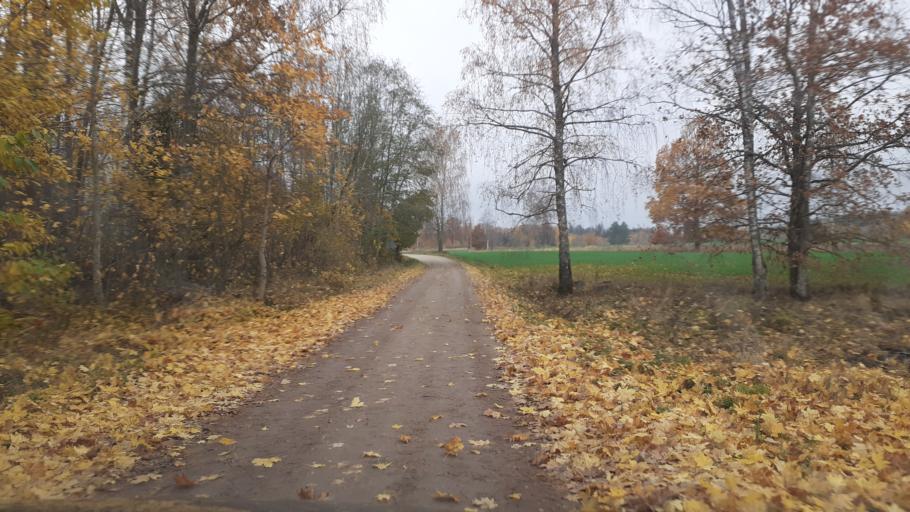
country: LV
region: Saldus Rajons
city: Saldus
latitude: 56.8773
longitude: 22.2957
